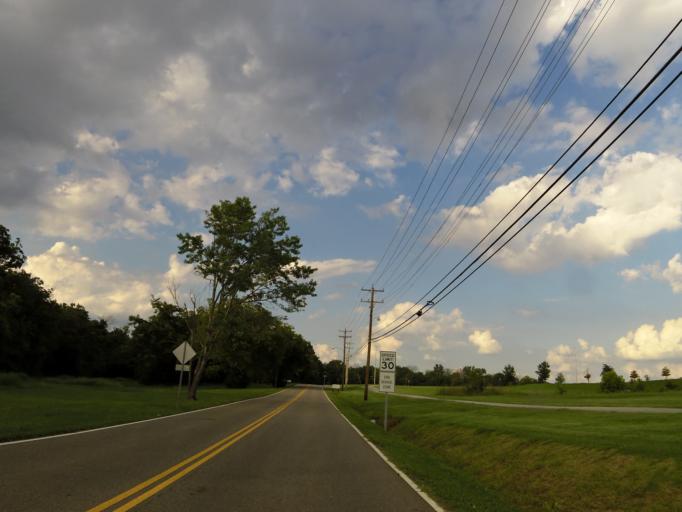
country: US
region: Tennessee
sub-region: Blount County
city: Alcoa
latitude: 35.7918
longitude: -83.9700
